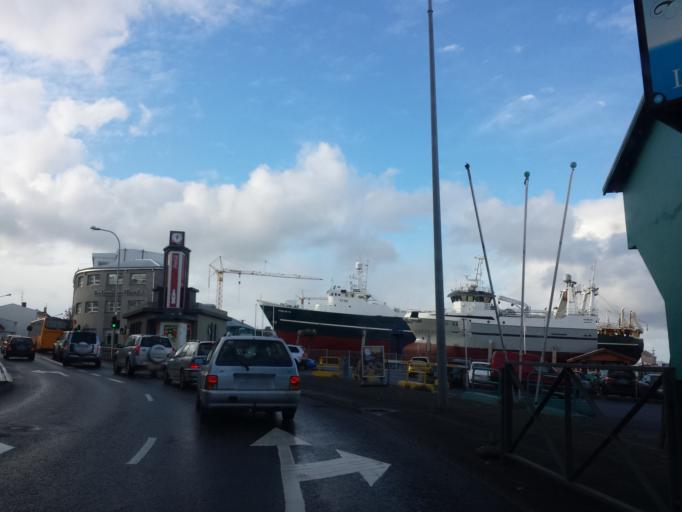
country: IS
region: Capital Region
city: Kopavogur
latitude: 64.1508
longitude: -21.9441
